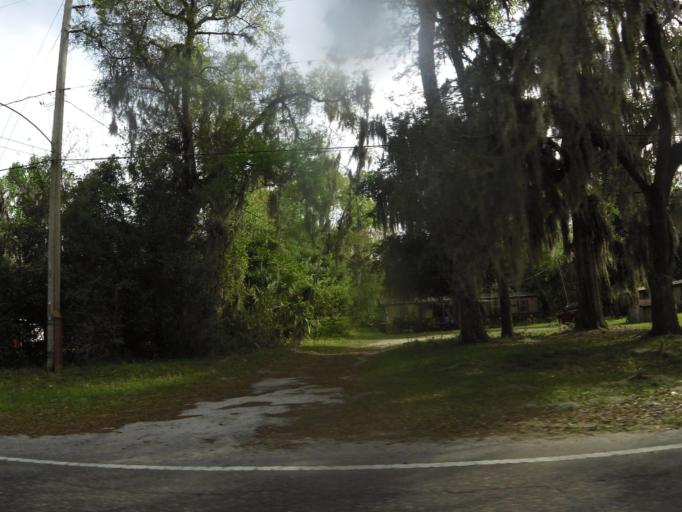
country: US
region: Florida
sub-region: Duval County
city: Jacksonville
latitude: 30.2985
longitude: -81.7591
